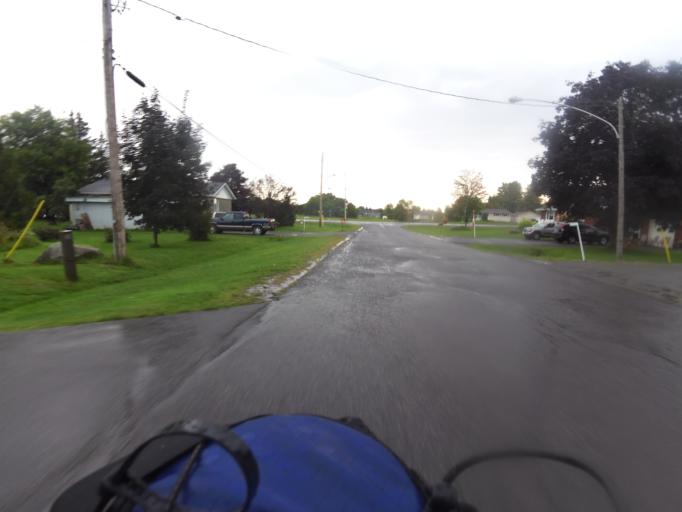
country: CA
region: Ontario
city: Ottawa
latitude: 45.2325
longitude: -75.4826
